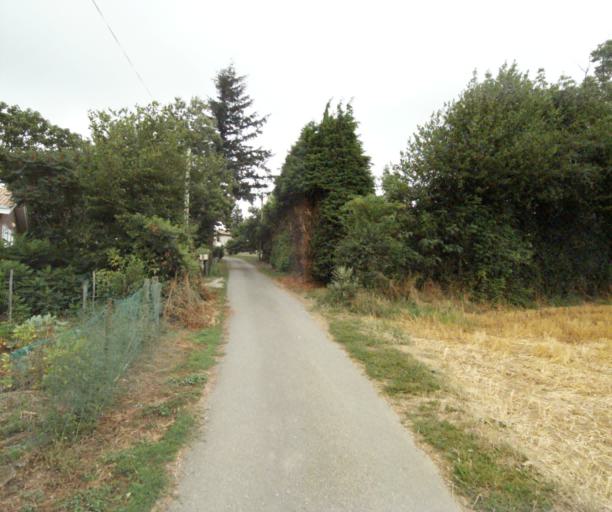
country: FR
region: Midi-Pyrenees
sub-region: Departement du Tarn
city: Soreze
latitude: 43.4029
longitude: 2.0494
